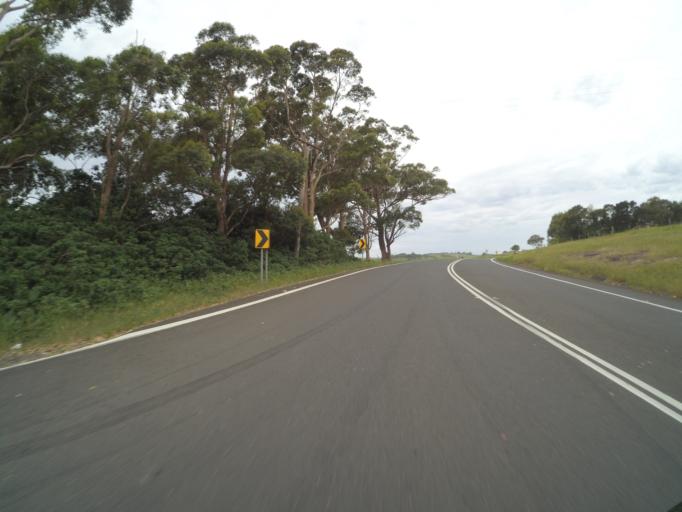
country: AU
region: New South Wales
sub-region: Kiama
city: Jamberoo
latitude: -34.6526
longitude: 150.8124
